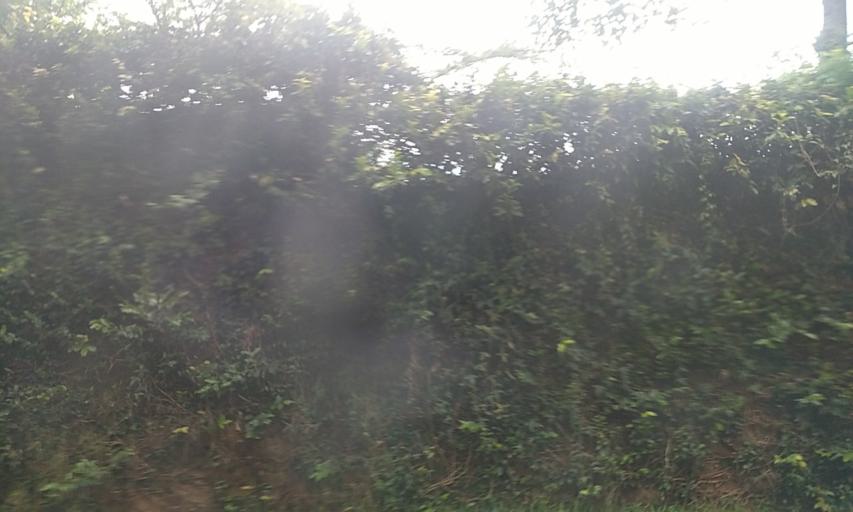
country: UG
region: Central Region
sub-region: Kampala District
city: Kampala
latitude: 0.3297
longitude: 32.5958
